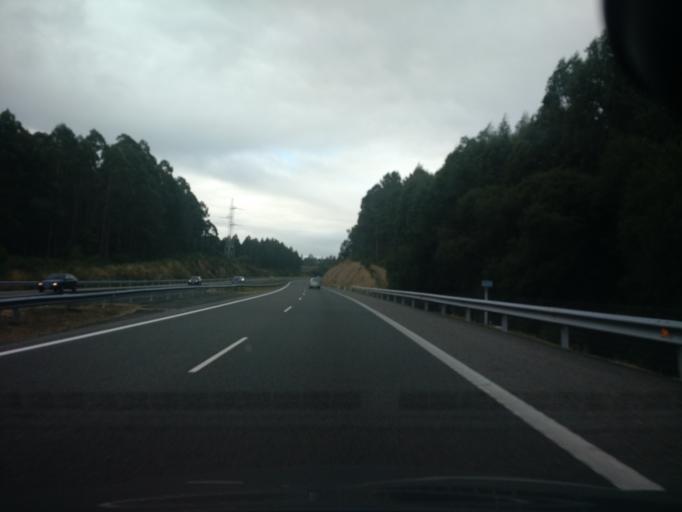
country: ES
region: Galicia
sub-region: Provincia da Coruna
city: Abegondo
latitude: 43.2208
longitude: -8.2754
